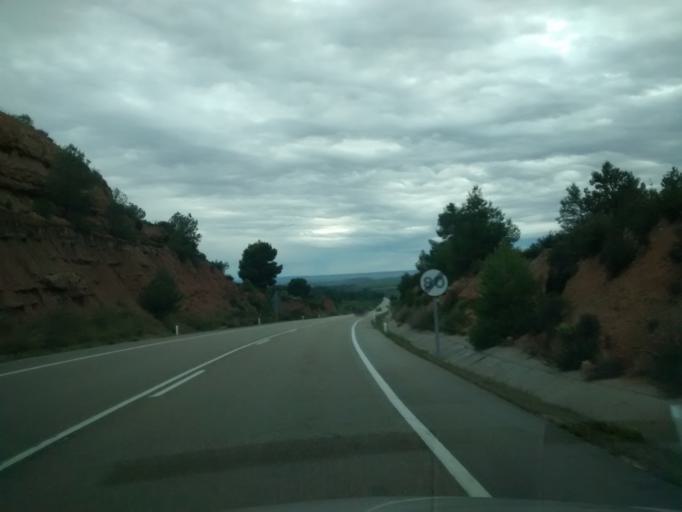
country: ES
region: Aragon
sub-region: Provincia de Zaragoza
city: Maella
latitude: 41.1602
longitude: 0.0829
